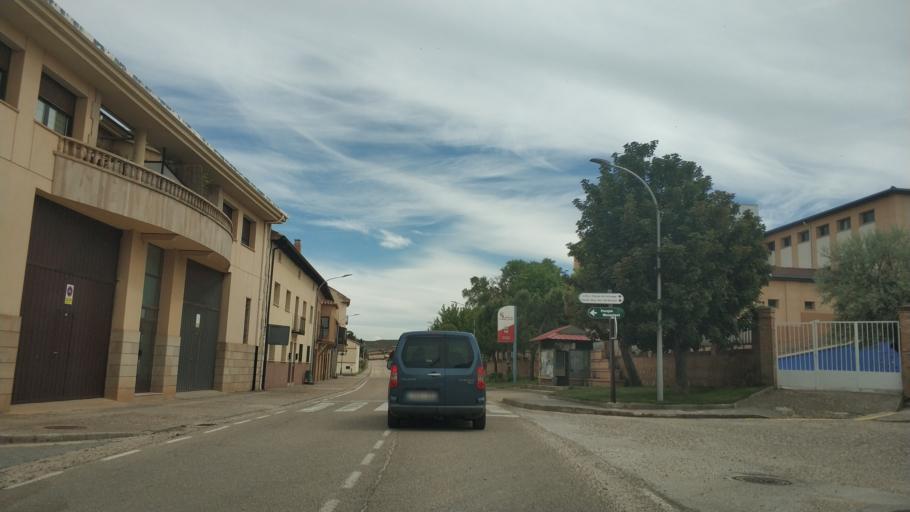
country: ES
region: Castille and Leon
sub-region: Provincia de Soria
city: Berlanga de Duero
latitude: 41.4650
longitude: -2.8629
